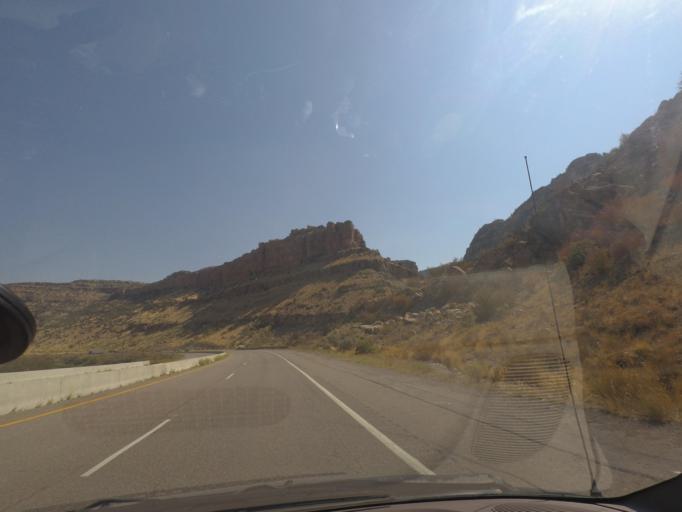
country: US
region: Colorado
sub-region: Mesa County
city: Palisade
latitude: 39.2075
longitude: -108.2599
